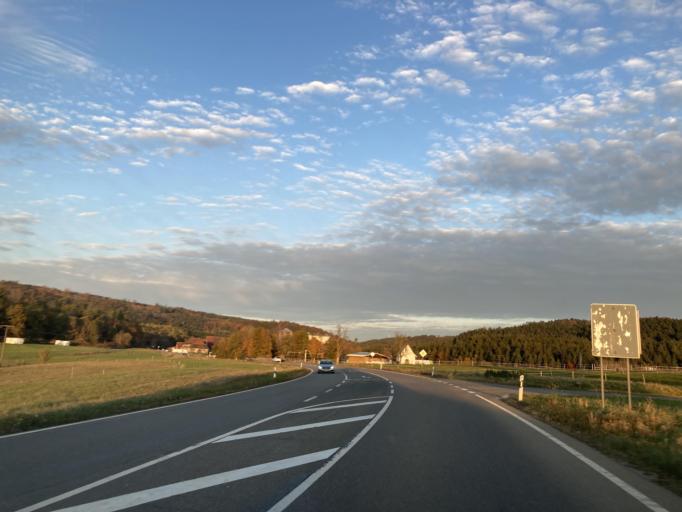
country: DE
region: Baden-Wuerttemberg
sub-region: Freiburg Region
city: Dietingen
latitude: 48.1815
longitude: 8.6571
